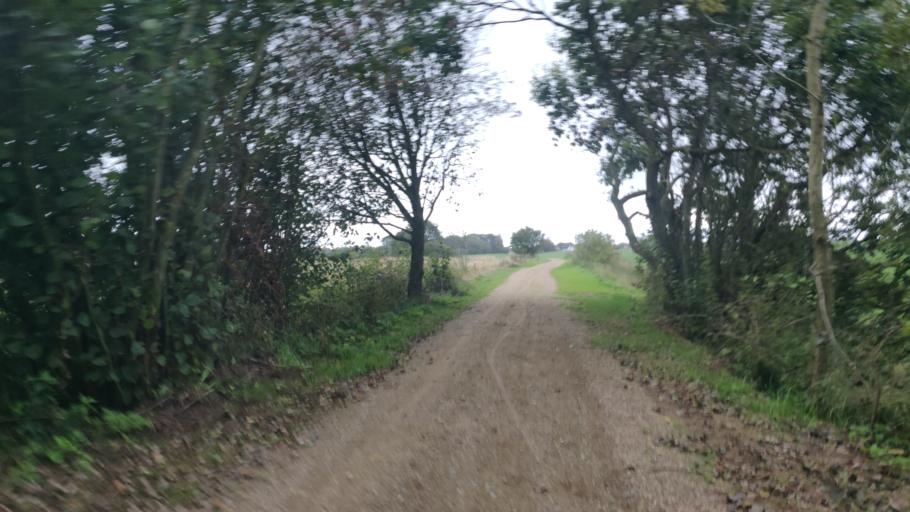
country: DK
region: South Denmark
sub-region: Kolding Kommune
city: Lunderskov
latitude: 55.5394
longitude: 9.3333
